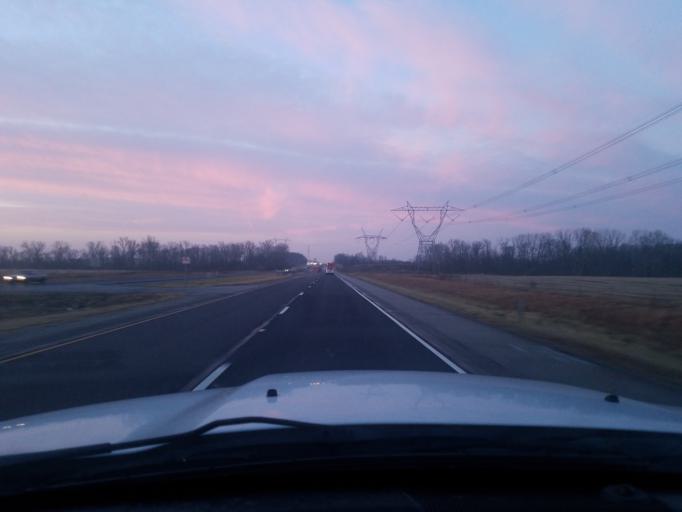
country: US
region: Indiana
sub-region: Huntington County
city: Roanoke
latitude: 40.9225
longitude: -85.3210
